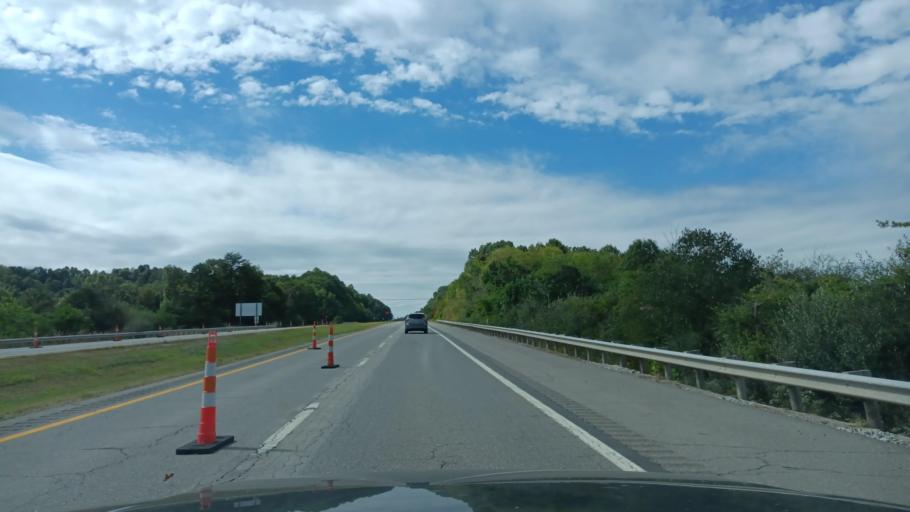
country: US
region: West Virginia
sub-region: Ritchie County
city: Harrisville
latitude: 39.2612
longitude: -81.1435
